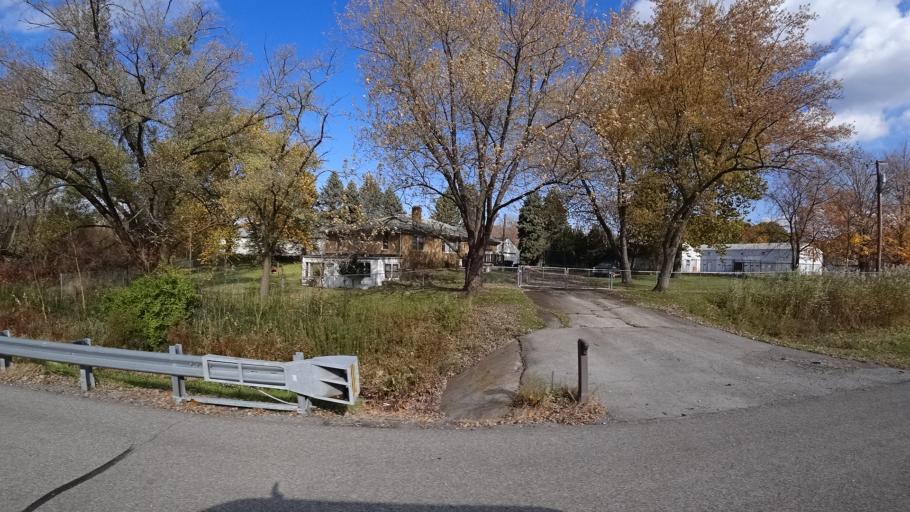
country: US
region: Indiana
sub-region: LaPorte County
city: Trail Creek
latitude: 41.7049
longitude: -86.8539
